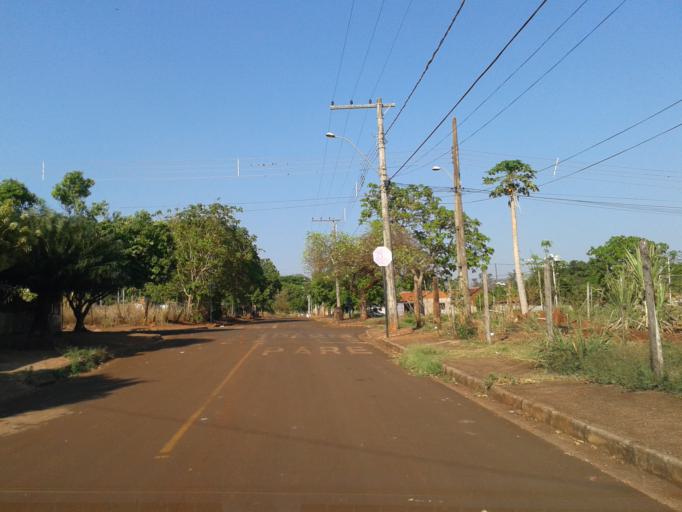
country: BR
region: Minas Gerais
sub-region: Ituiutaba
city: Ituiutaba
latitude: -18.9464
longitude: -49.4610
